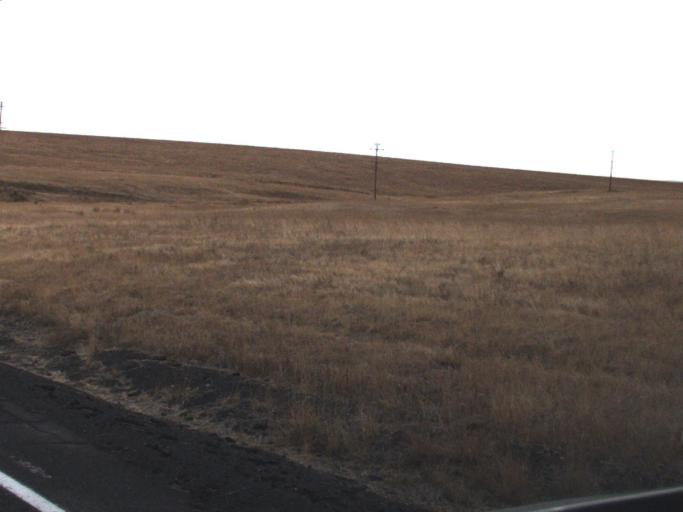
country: US
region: Washington
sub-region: Okanogan County
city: Coulee Dam
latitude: 47.6125
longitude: -118.7461
